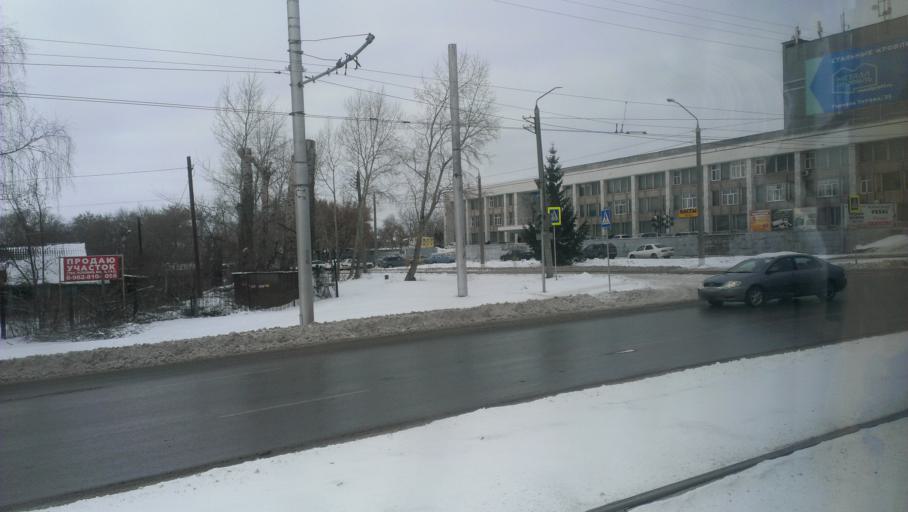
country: RU
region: Altai Krai
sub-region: Gorod Barnaulskiy
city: Barnaul
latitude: 53.3823
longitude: 83.7131
